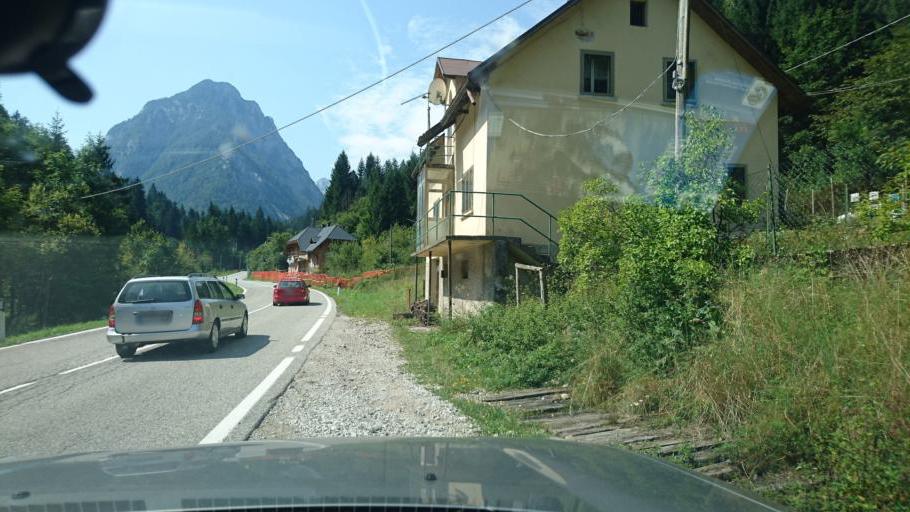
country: IT
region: Friuli Venezia Giulia
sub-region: Provincia di Udine
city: Tarvisio
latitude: 46.4832
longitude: 13.5787
